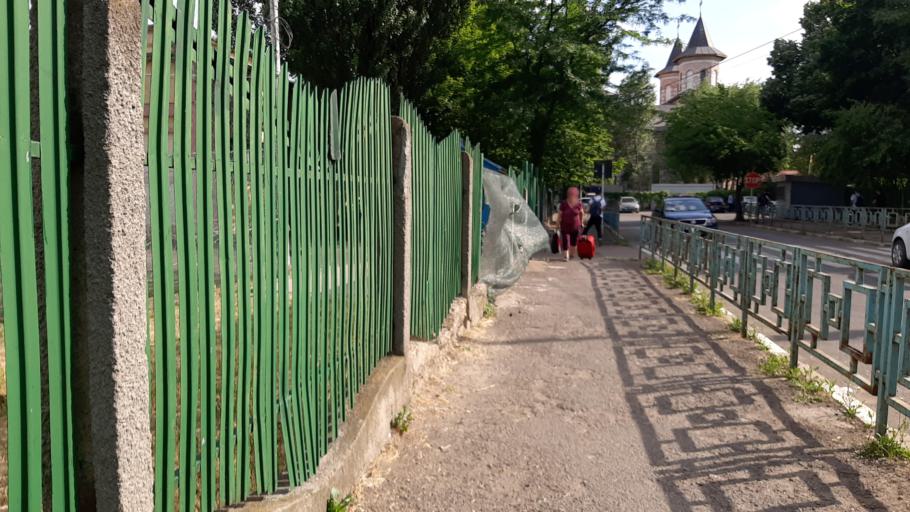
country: RO
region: Galati
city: Galati
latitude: 45.4423
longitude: 28.0266
